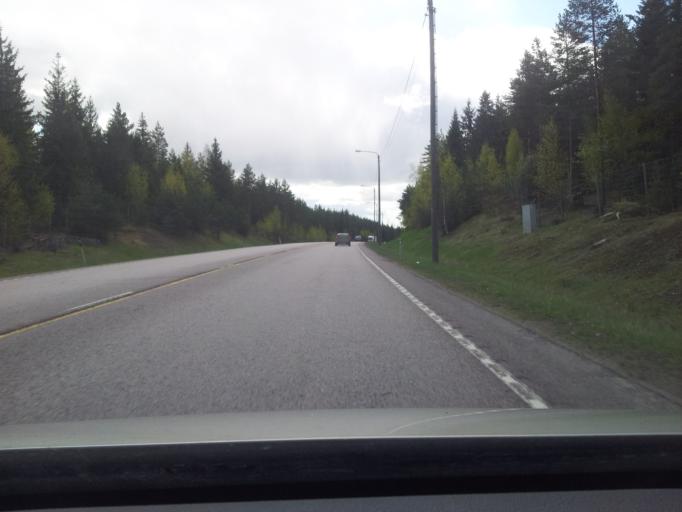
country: FI
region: Uusimaa
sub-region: Loviisa
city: Perna
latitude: 60.5091
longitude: 25.9658
